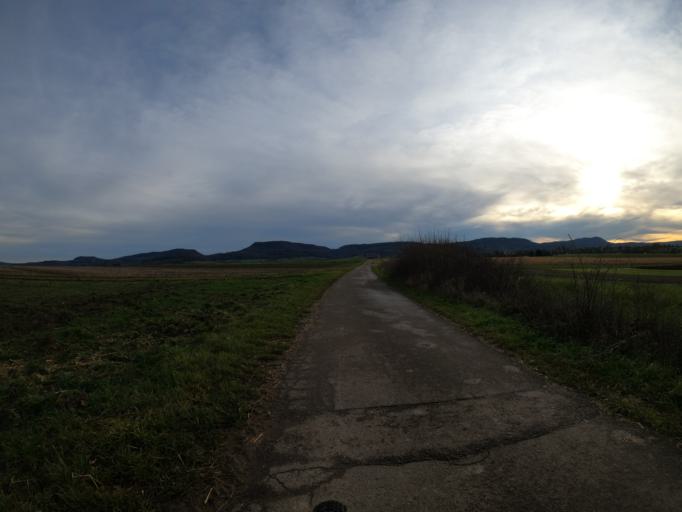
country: DE
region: Baden-Wuerttemberg
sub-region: Regierungsbezirk Stuttgart
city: Heiningen
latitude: 48.6733
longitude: 9.6494
